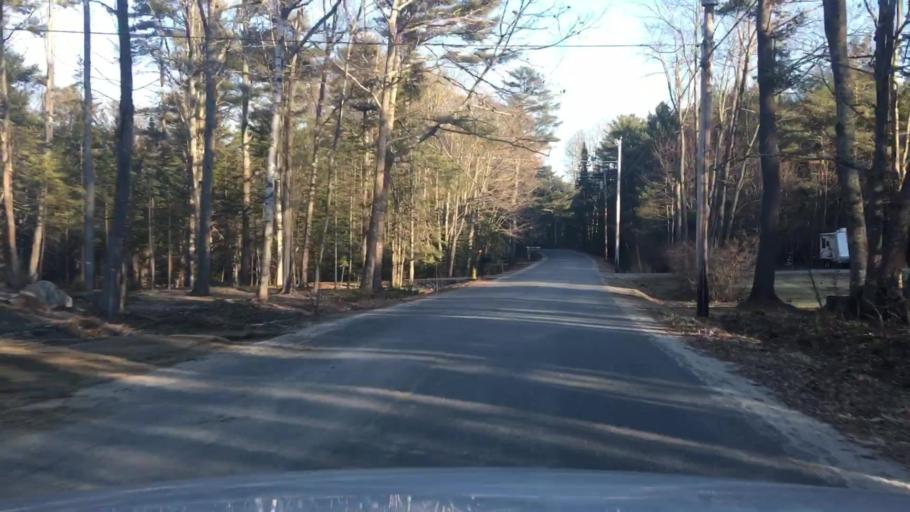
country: US
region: Maine
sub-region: Cumberland County
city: Brunswick
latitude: 43.8862
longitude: -69.9140
